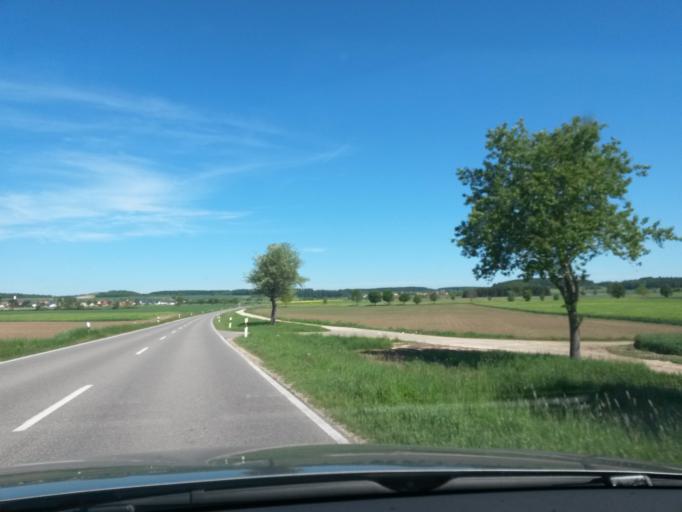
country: DE
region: Baden-Wuerttemberg
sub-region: Tuebingen Region
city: Gammertingen
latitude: 48.2482
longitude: 9.2861
